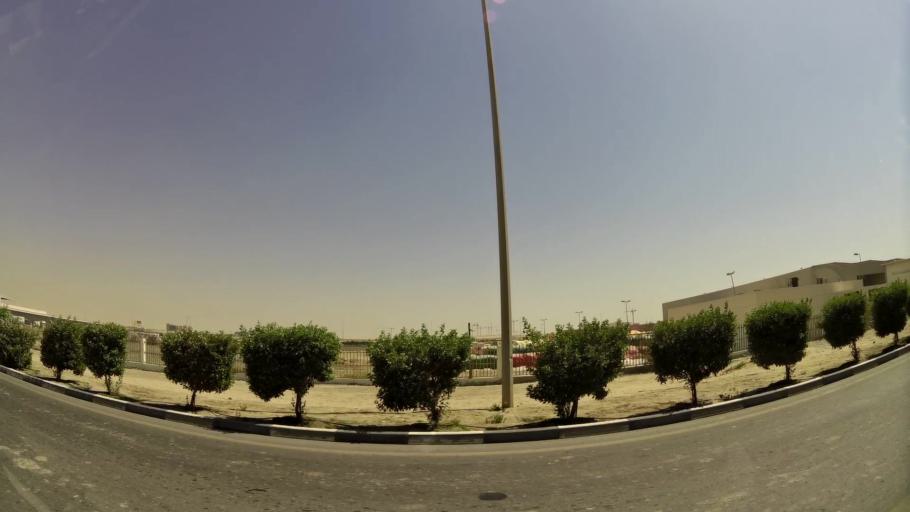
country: AE
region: Dubai
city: Dubai
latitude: 24.9748
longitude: 55.1578
